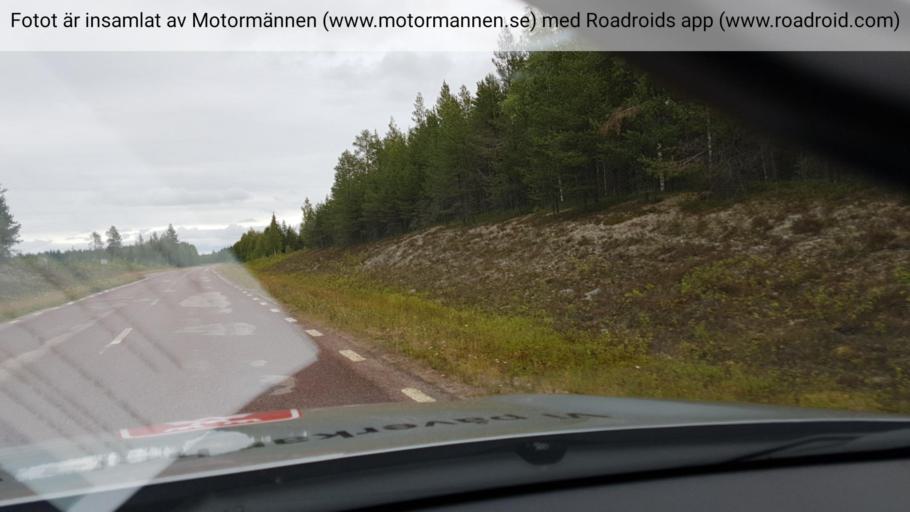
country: SE
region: Norrbotten
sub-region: Pajala Kommun
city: Pajala
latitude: 67.1409
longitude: 22.6153
